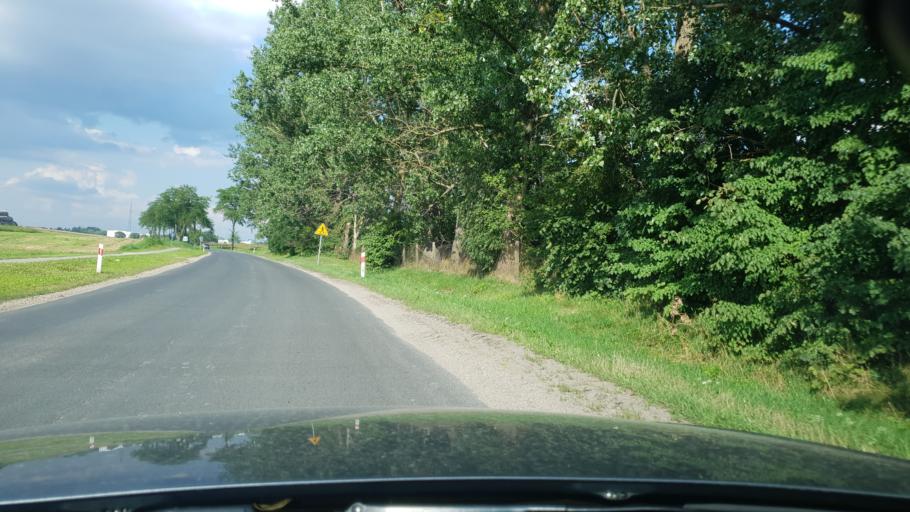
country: PL
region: Kujawsko-Pomorskie
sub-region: Powiat wabrzeski
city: Wabrzezno
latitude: 53.2642
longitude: 18.9056
